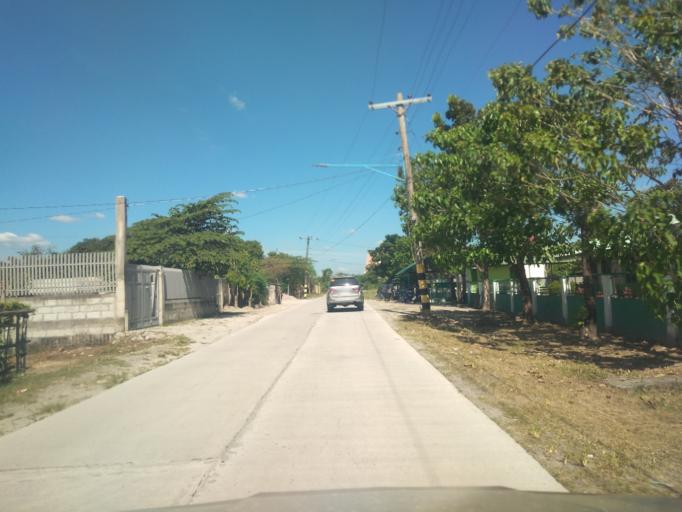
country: PH
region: Central Luzon
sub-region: Province of Pampanga
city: Bacolor
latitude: 15.0240
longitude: 120.6376
